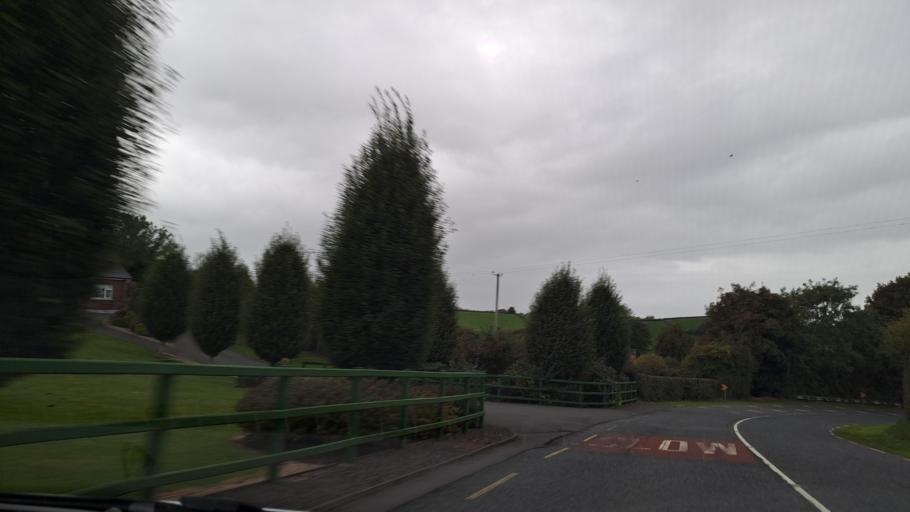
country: IE
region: Ulster
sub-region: County Monaghan
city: Monaghan
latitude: 54.2244
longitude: -6.9540
